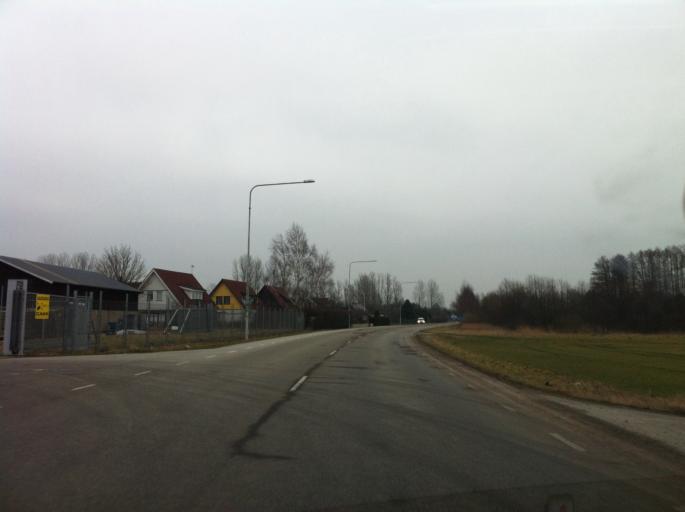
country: SE
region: Skane
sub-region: Landskrona
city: Asmundtorp
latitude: 55.8836
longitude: 12.9084
